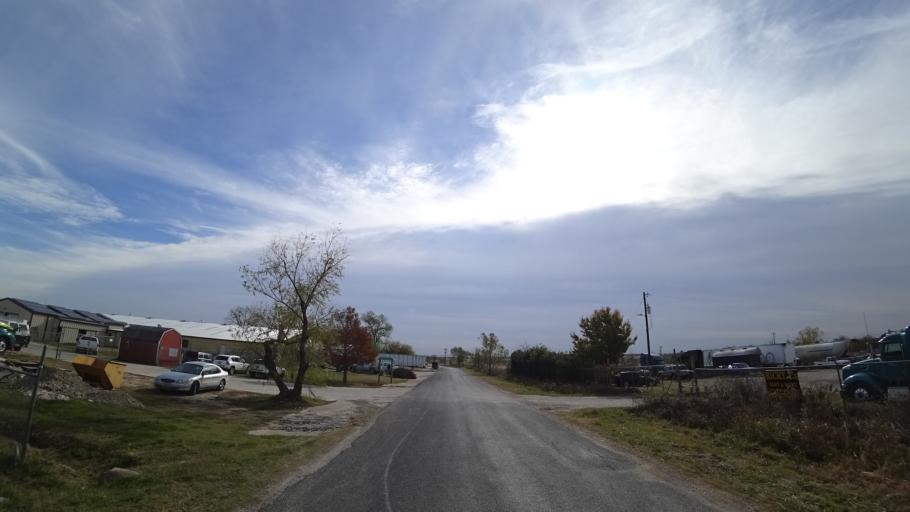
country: US
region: Texas
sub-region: Travis County
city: Onion Creek
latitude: 30.1537
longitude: -97.6980
